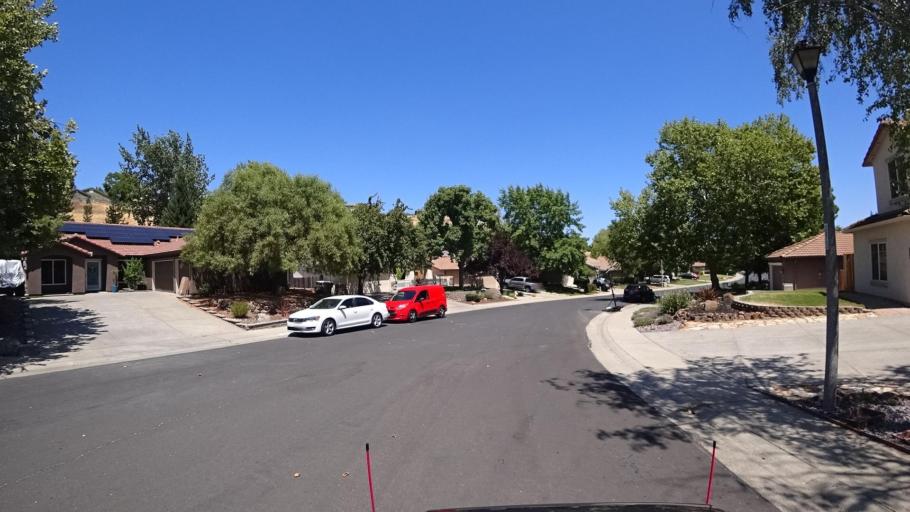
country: US
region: California
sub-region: Placer County
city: Rocklin
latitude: 38.8228
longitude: -121.2672
